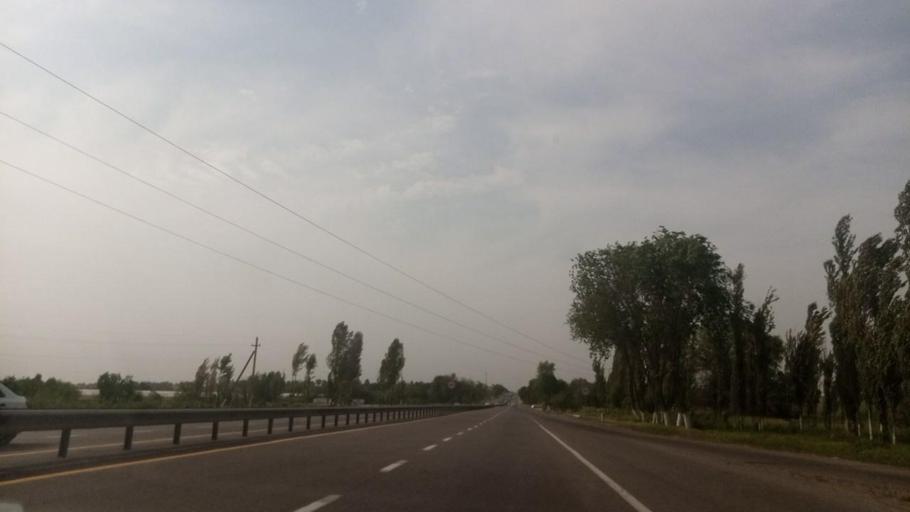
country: UZ
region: Toshkent
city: Tuytepa
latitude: 41.0722
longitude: 69.4761
